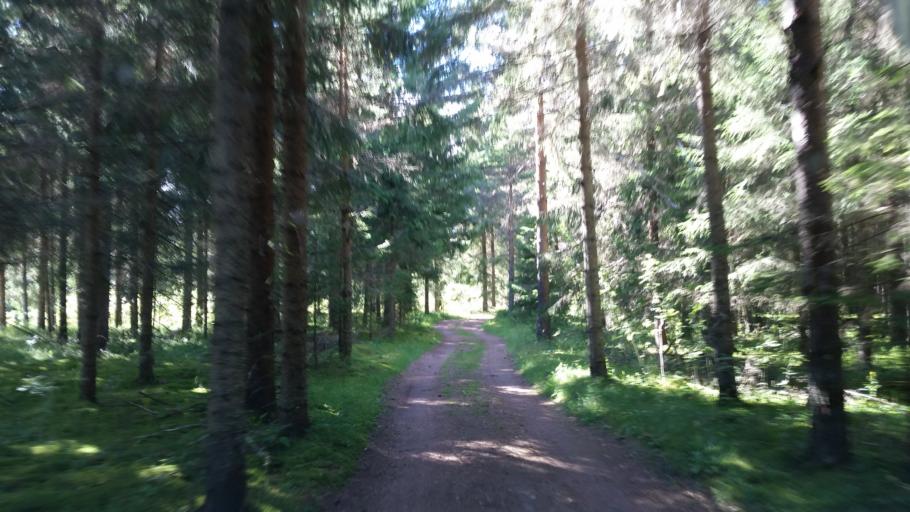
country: SE
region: Gaevleborg
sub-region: Ljusdals Kommun
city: Ljusdal
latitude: 61.9715
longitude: 16.3298
